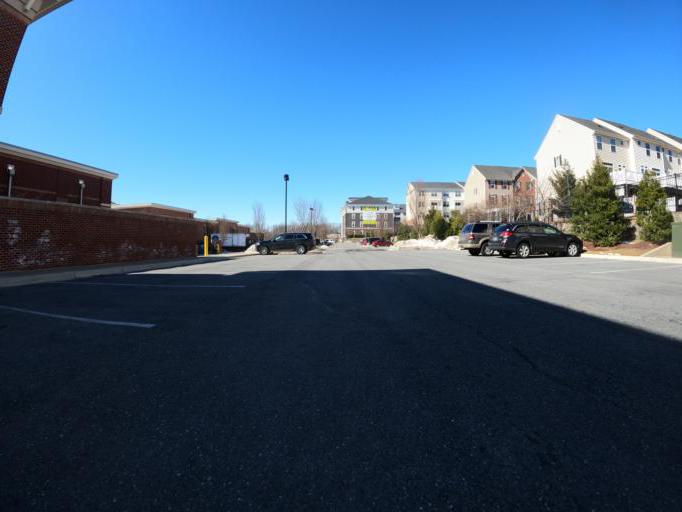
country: US
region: Maryland
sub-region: Montgomery County
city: Clarksburg
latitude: 39.2301
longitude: -77.2487
